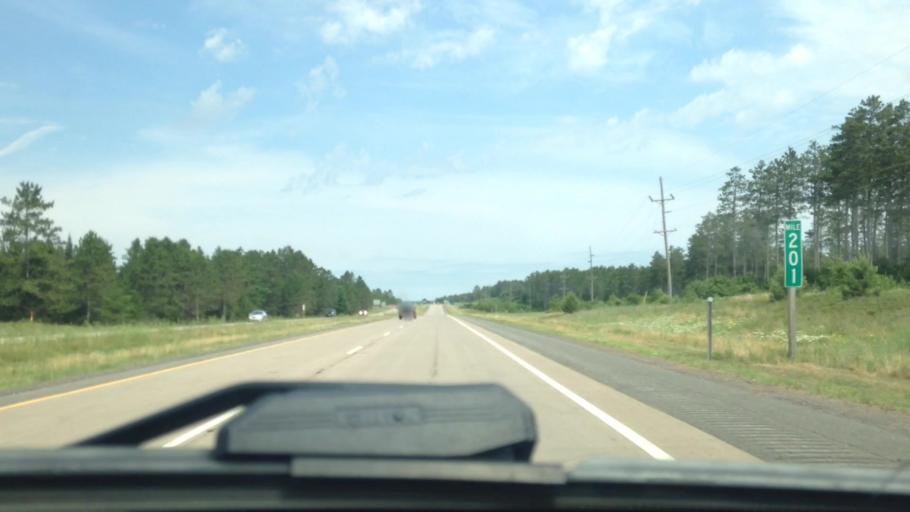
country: US
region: Wisconsin
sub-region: Douglas County
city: Lake Nebagamon
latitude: 46.3074
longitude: -91.8117
